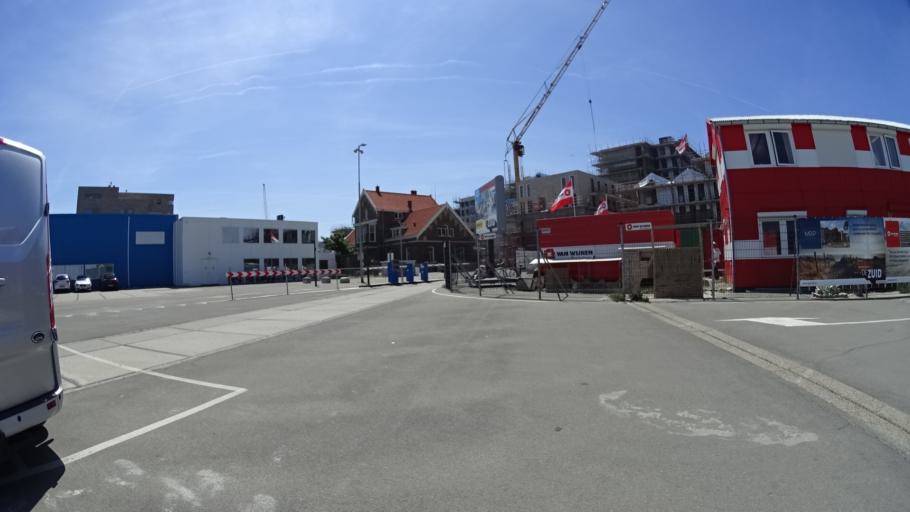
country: NL
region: South Holland
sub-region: Gemeente Den Haag
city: Scheveningen
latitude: 52.0963
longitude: 4.2611
